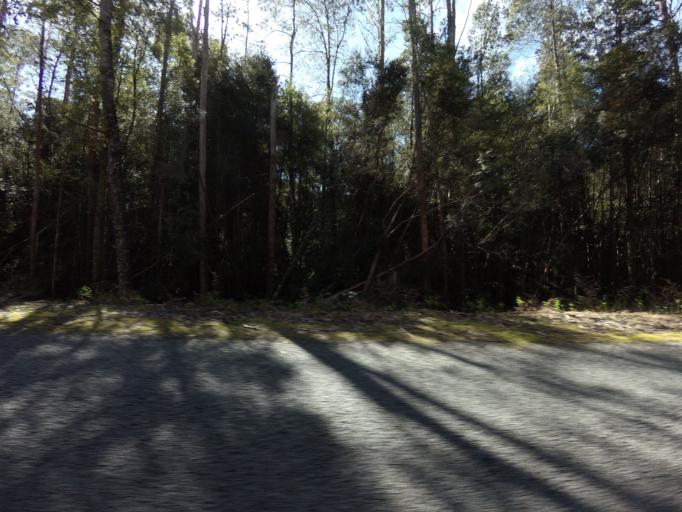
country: AU
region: Tasmania
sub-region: Huon Valley
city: Geeveston
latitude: -42.7777
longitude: 146.3983
